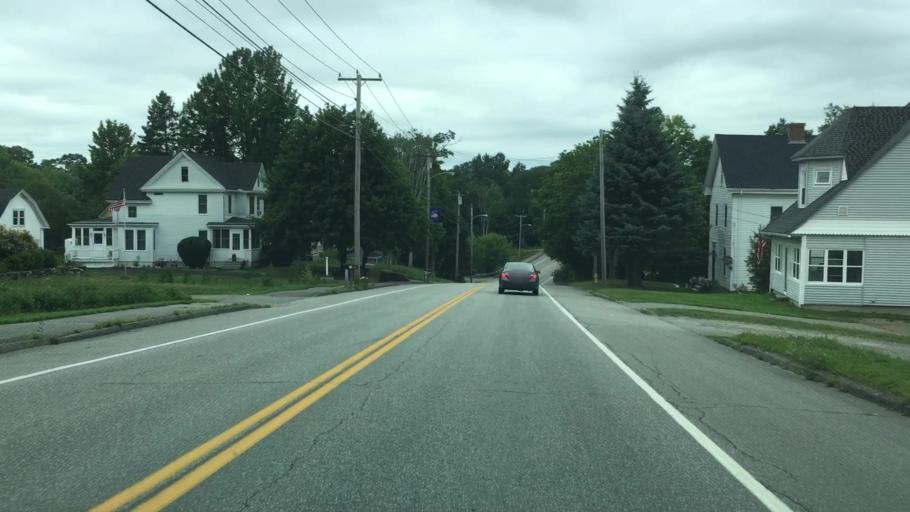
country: US
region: Maine
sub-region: Penobscot County
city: Hampden
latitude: 44.7346
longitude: -68.8413
